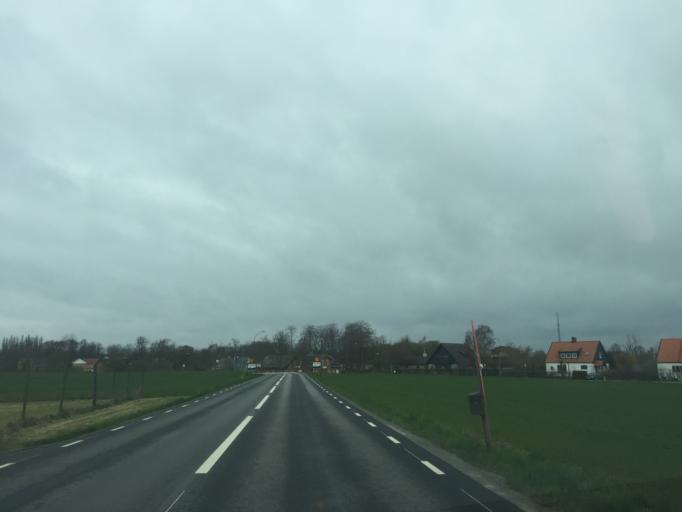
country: SE
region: Skane
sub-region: Skurups Kommun
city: Skivarp
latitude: 55.4256
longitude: 13.5870
